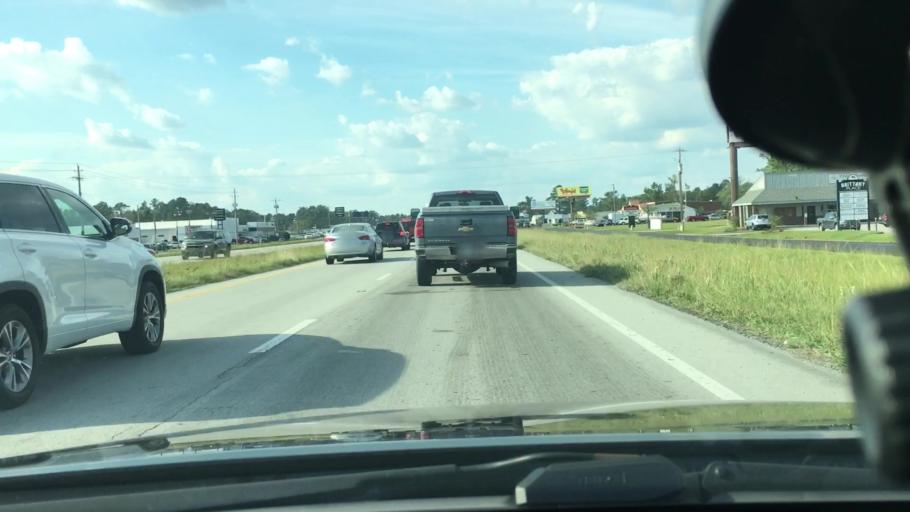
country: US
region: North Carolina
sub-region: Craven County
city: James City
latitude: 35.0685
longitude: -77.0243
